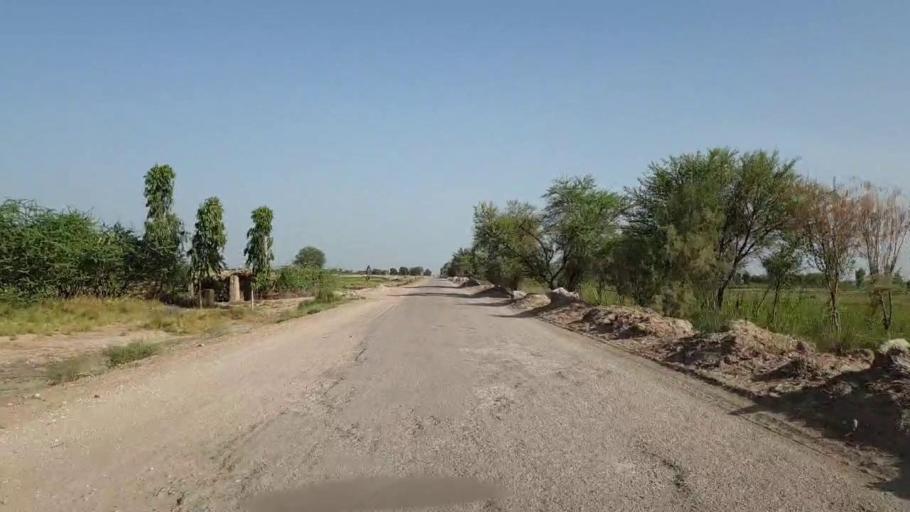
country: PK
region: Sindh
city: Nawabshah
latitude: 26.1601
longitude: 68.4441
